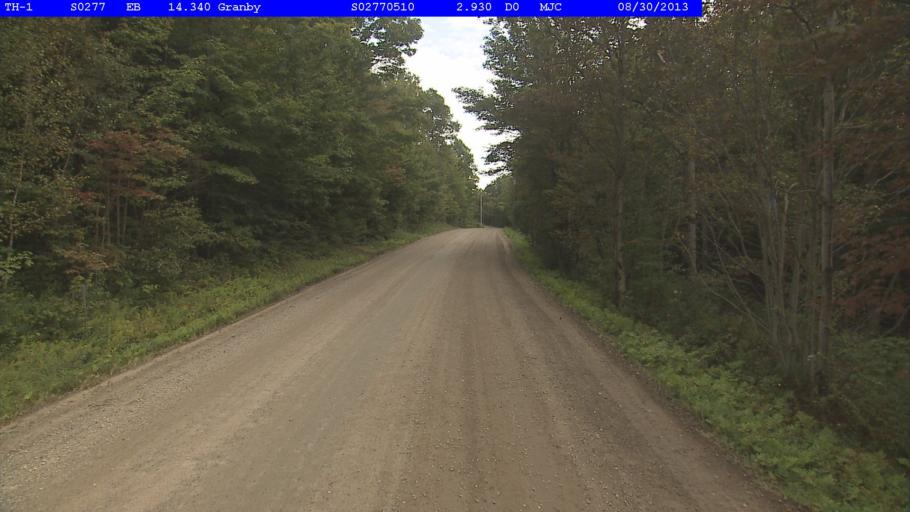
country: US
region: Vermont
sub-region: Essex County
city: Guildhall
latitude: 44.5754
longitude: -71.7097
